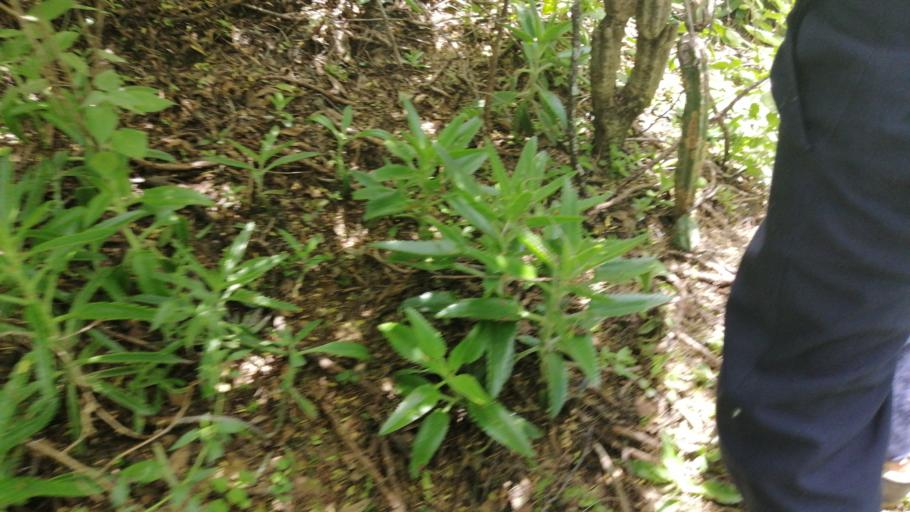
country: CO
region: Boyaca
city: Soata
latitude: 6.2861
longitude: -72.6494
